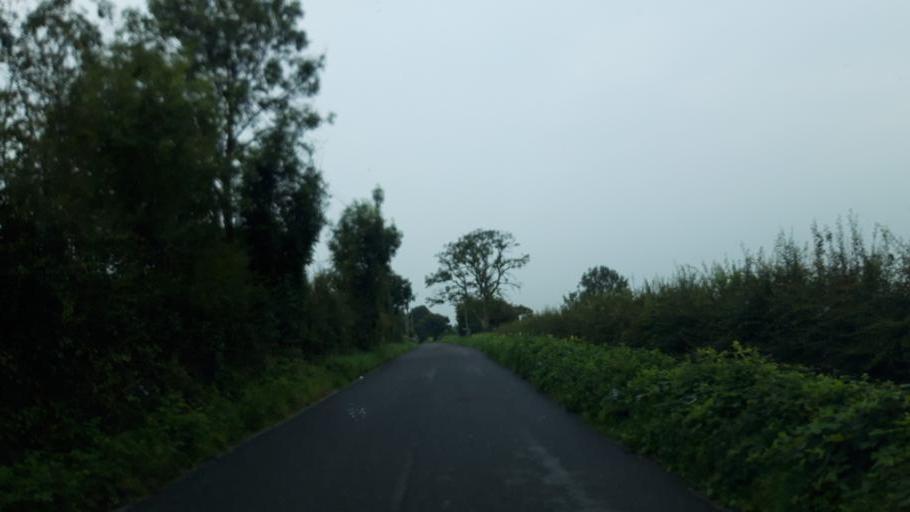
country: IE
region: Leinster
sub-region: Kilkenny
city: Thomastown
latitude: 52.5992
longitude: -7.1529
